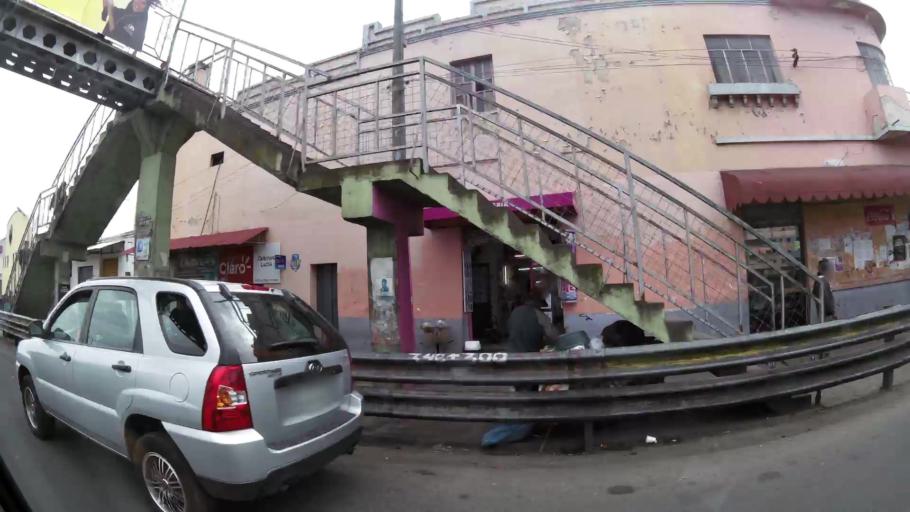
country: EC
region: Cotopaxi
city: Latacunga
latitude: -0.9330
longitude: -78.6211
